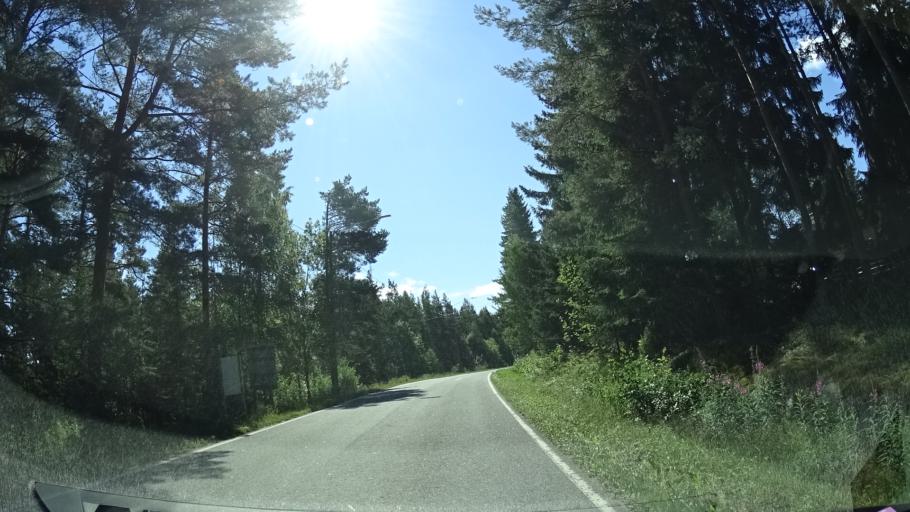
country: FI
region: Varsinais-Suomi
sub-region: Turku
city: Velkua
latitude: 60.5111
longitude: 21.7497
